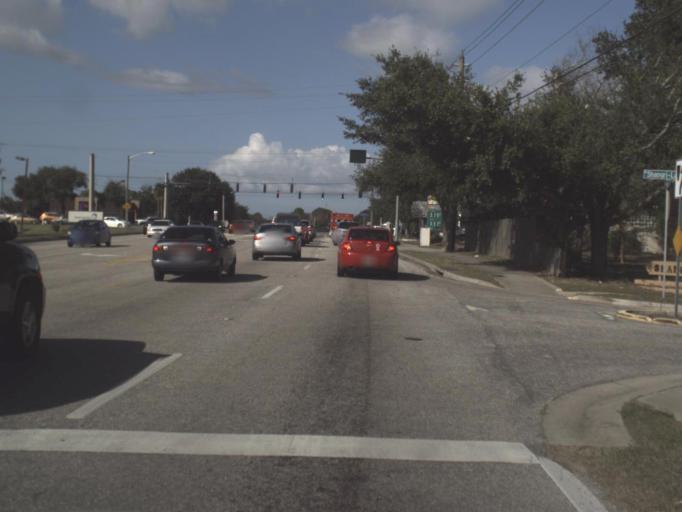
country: US
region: Florida
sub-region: Volusia County
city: South Daytona
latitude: 29.1699
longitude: -81.0379
